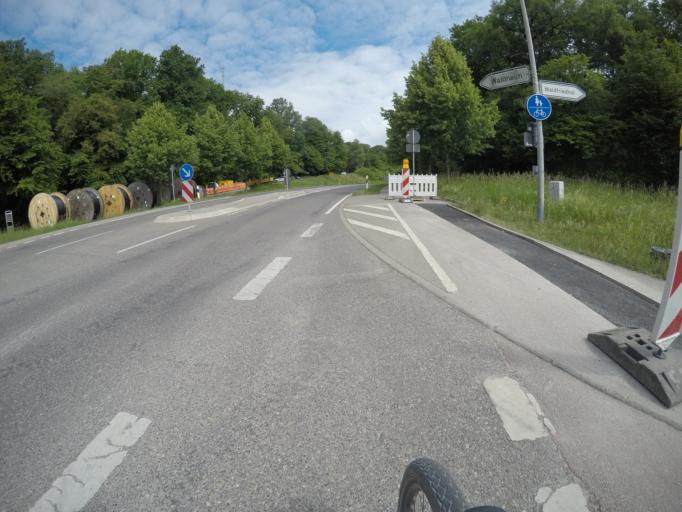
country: DE
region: Baden-Wuerttemberg
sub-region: Regierungsbezirk Stuttgart
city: Notzingen
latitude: 48.6607
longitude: 9.4576
